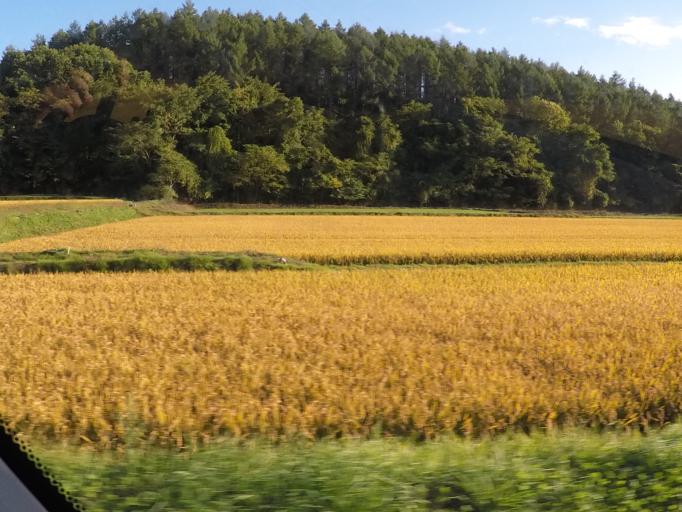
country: JP
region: Hokkaido
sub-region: Asahikawa-shi
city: Asahikawa
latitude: 43.6211
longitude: 142.4975
